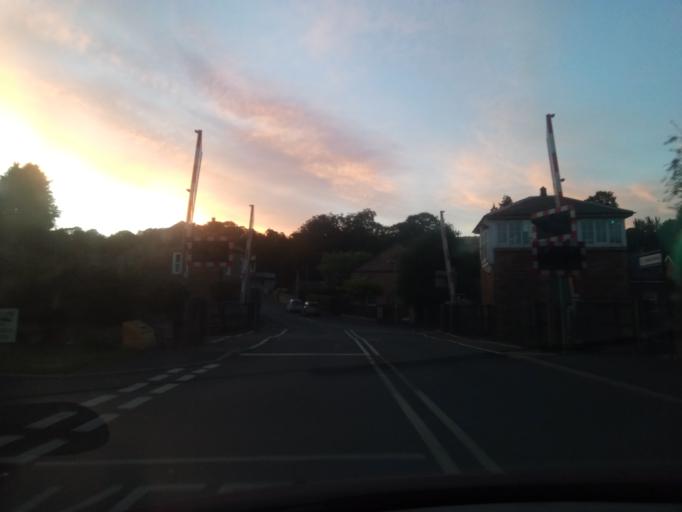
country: GB
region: England
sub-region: Northumberland
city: Bardon Mill
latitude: 54.9747
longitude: -2.2482
